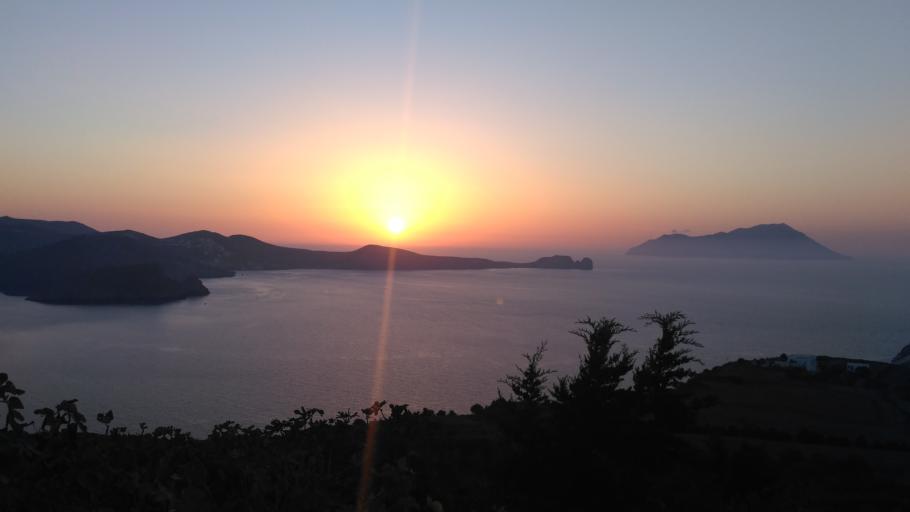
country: GR
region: South Aegean
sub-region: Nomos Kykladon
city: Milos
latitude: 36.7441
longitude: 24.4214
